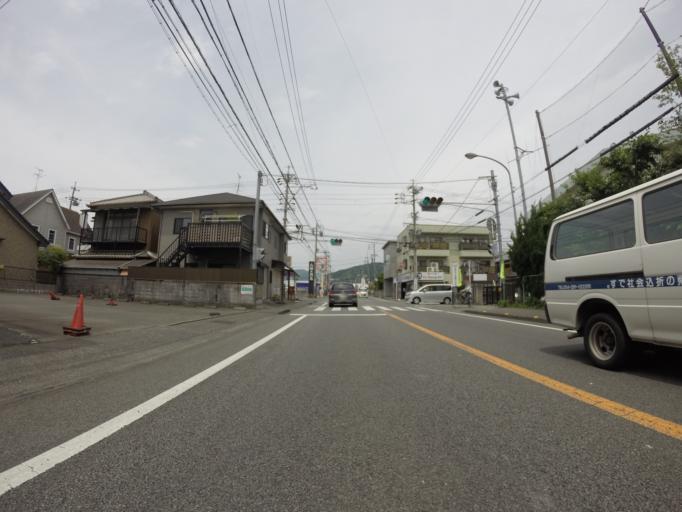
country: JP
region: Shizuoka
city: Shizuoka-shi
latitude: 34.9800
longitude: 138.3439
